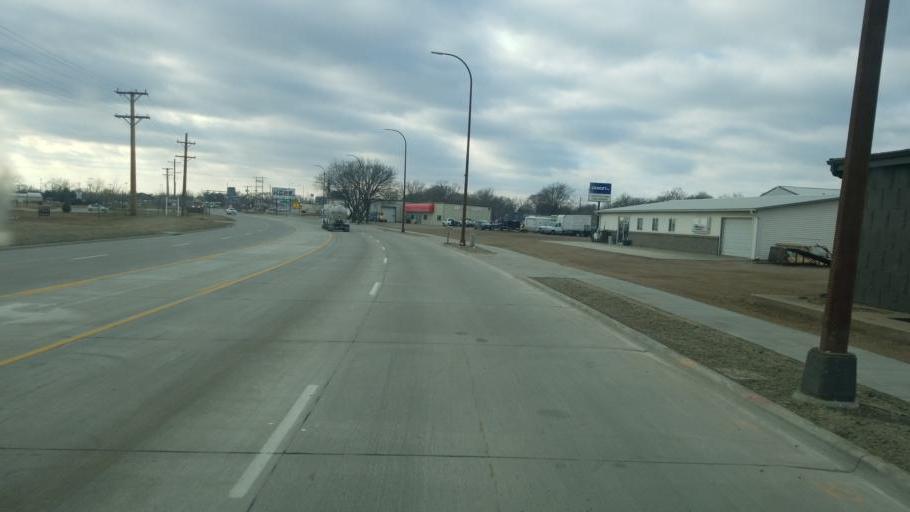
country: US
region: South Dakota
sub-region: Yankton County
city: Yankton
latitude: 42.8734
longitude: -97.3790
